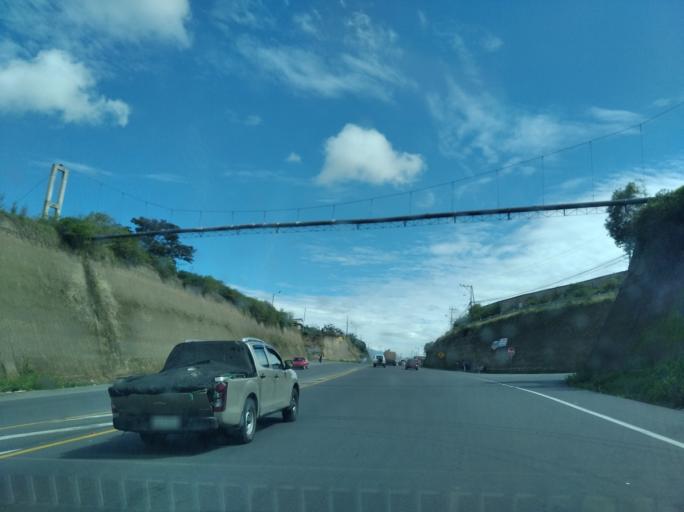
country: EC
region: Pichincha
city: Sangolqui
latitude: -0.1801
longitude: -78.3299
